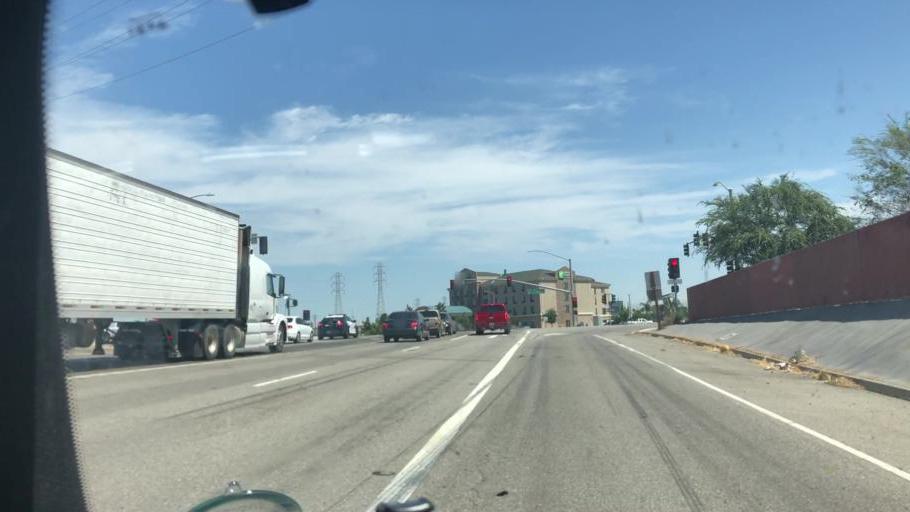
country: US
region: California
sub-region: Kern County
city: Greenacres
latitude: 35.4406
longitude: -119.0816
